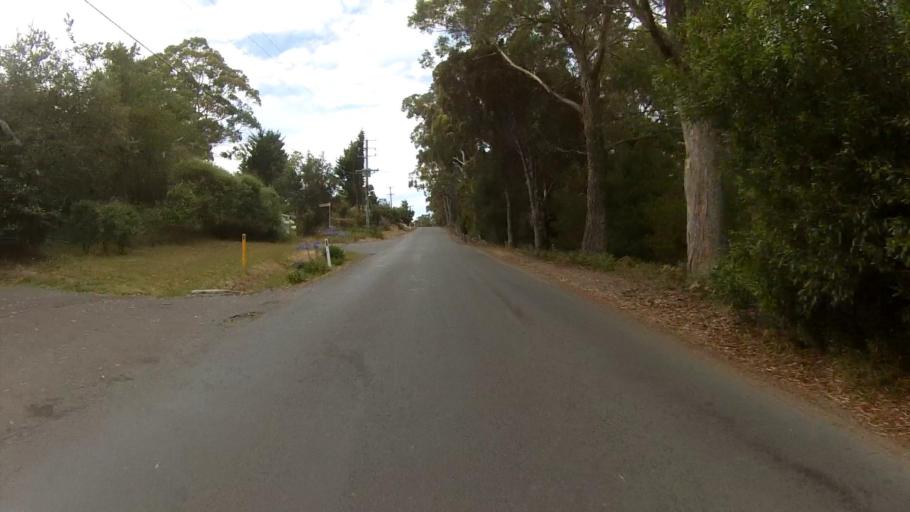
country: AU
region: Tasmania
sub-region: Kingborough
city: Blackmans Bay
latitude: -43.0249
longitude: 147.2966
